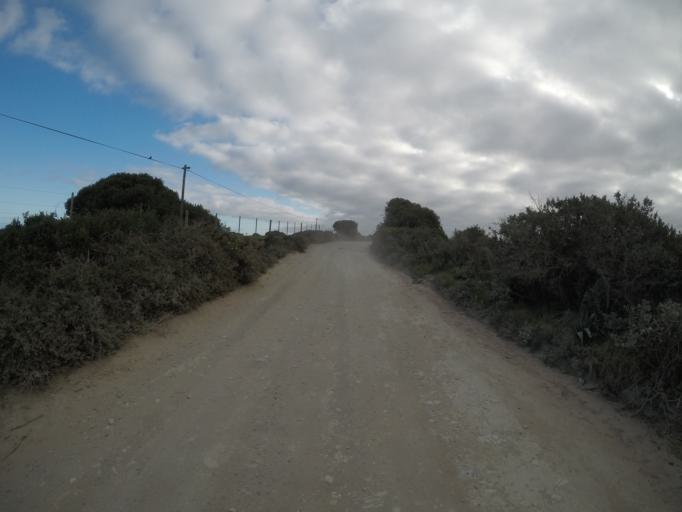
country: ZA
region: Western Cape
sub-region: Eden District Municipality
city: Riversdale
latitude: -34.4190
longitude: 21.3391
